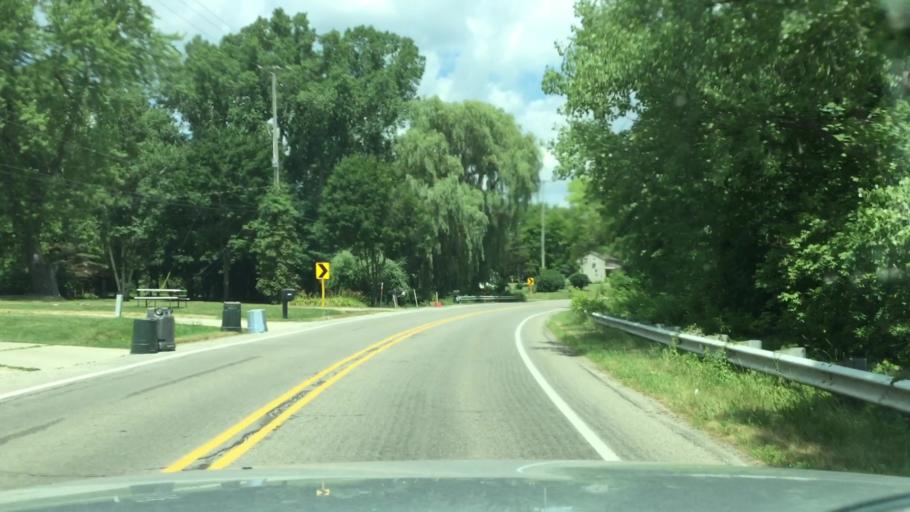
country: US
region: Michigan
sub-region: Genesee County
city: Flushing
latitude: 43.0723
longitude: -83.8728
